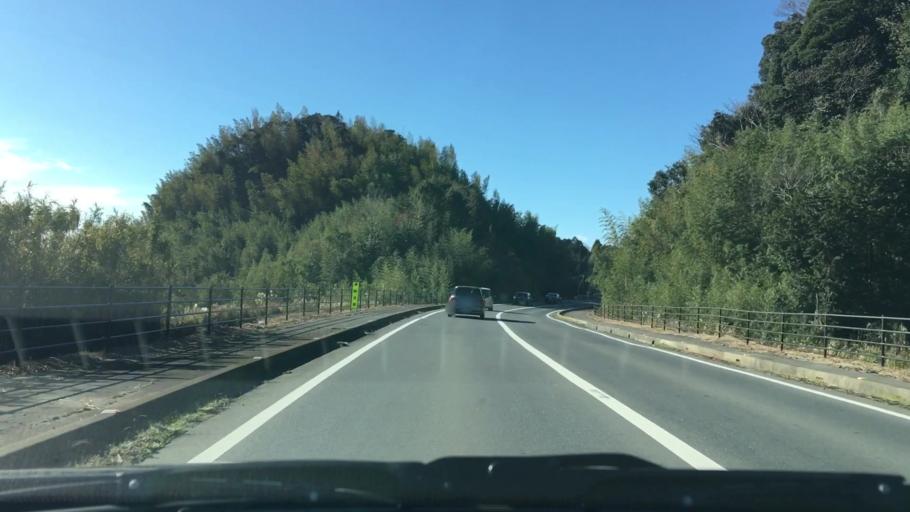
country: JP
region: Chiba
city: Omigawa
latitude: 35.8393
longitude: 140.5641
